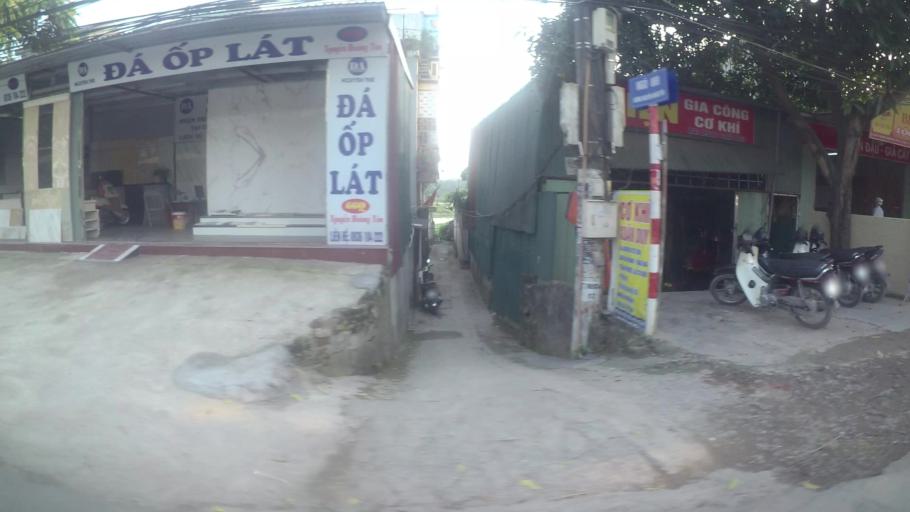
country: VN
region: Ha Noi
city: Tay Ho
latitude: 21.0770
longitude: 105.7918
